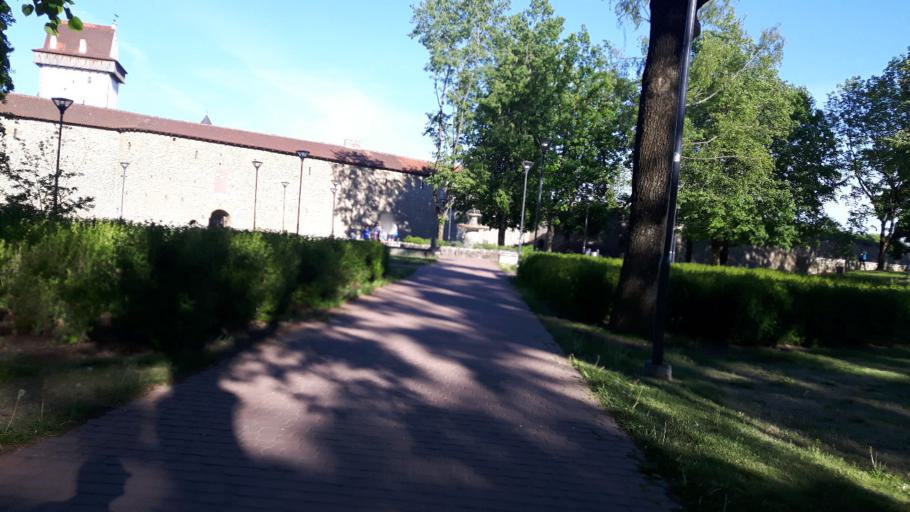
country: EE
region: Ida-Virumaa
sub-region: Narva linn
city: Narva
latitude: 59.3757
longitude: 28.1973
